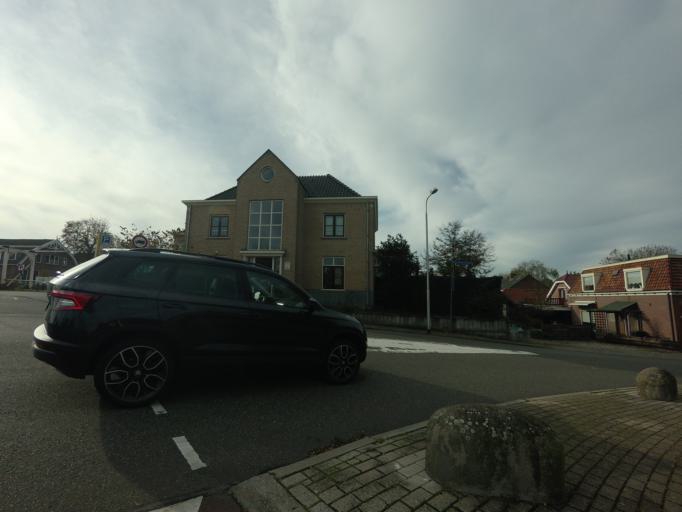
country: NL
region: South Holland
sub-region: Gemeente Nieuwkoop
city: Nieuwkoop
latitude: 52.1532
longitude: 4.7841
